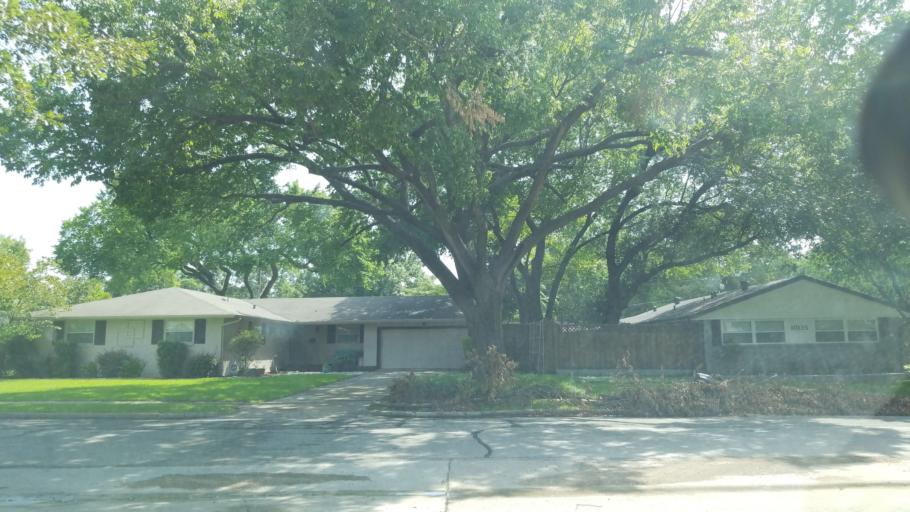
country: US
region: Texas
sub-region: Dallas County
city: Farmers Branch
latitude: 32.8850
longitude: -96.8576
